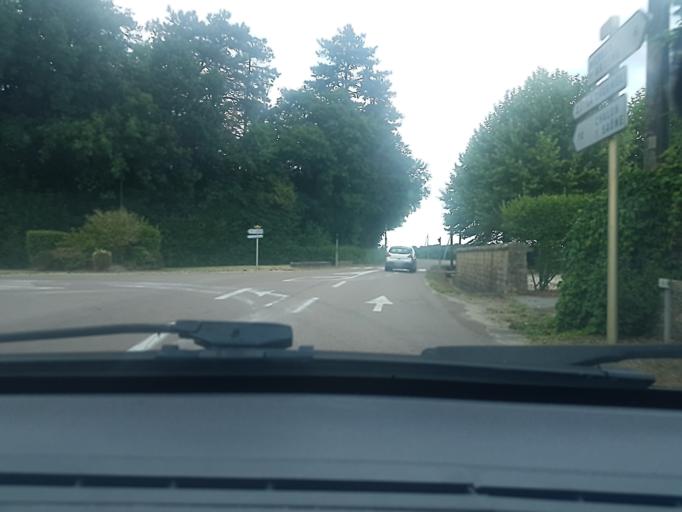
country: FR
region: Bourgogne
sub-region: Departement de Saone-et-Loire
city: Buxy
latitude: 46.7081
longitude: 4.7740
